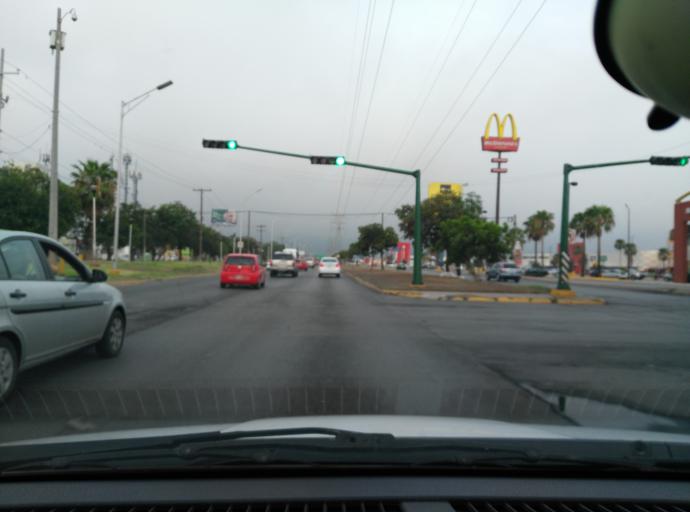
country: MX
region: Nuevo Leon
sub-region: San Nicolas de los Garza
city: San Nicolas de los Garza
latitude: 25.7701
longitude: -100.2725
